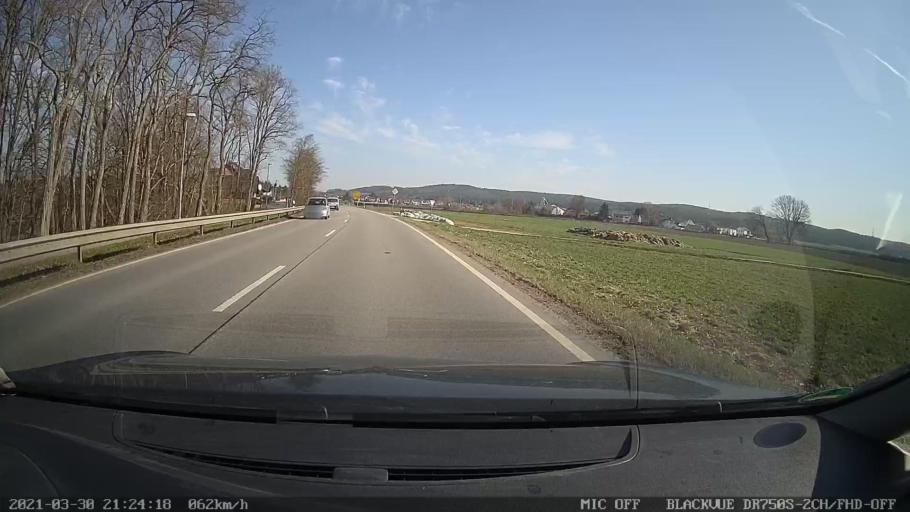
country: DE
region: Bavaria
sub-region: Upper Palatinate
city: Zeitlarn
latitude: 49.0858
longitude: 12.1187
